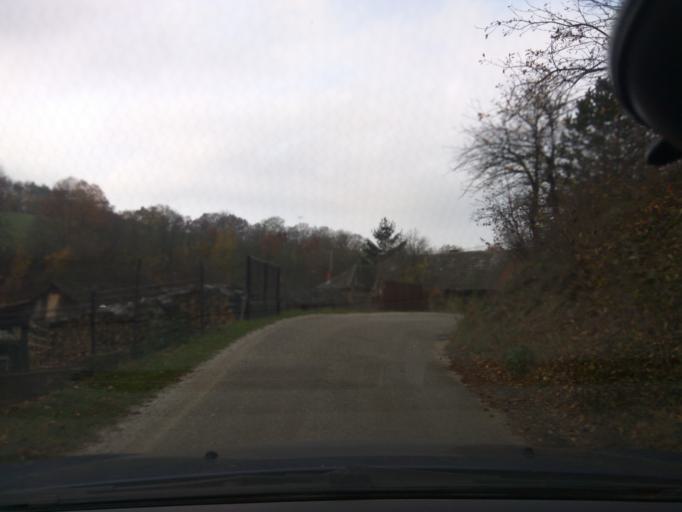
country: SK
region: Trnavsky
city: Vrbove
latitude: 48.6917
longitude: 17.6920
